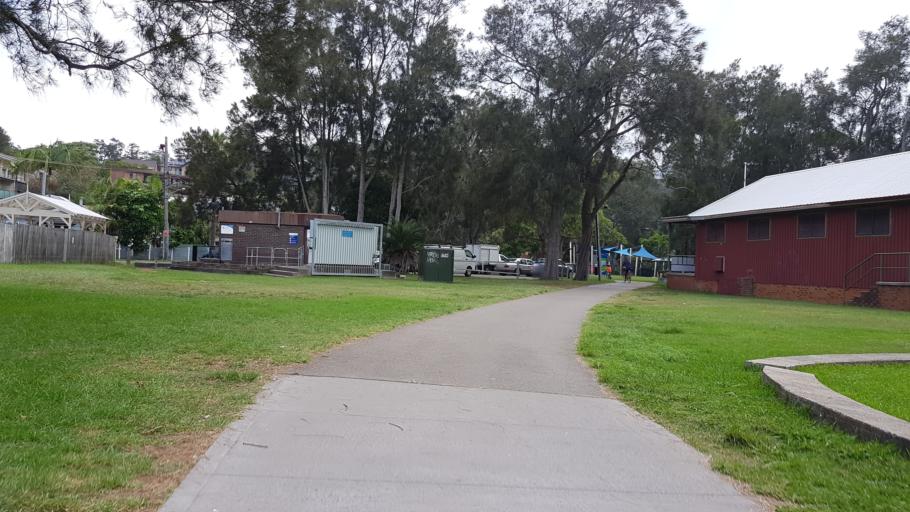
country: AU
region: New South Wales
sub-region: Warringah
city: Narrabeen
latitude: -33.7201
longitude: 151.2952
